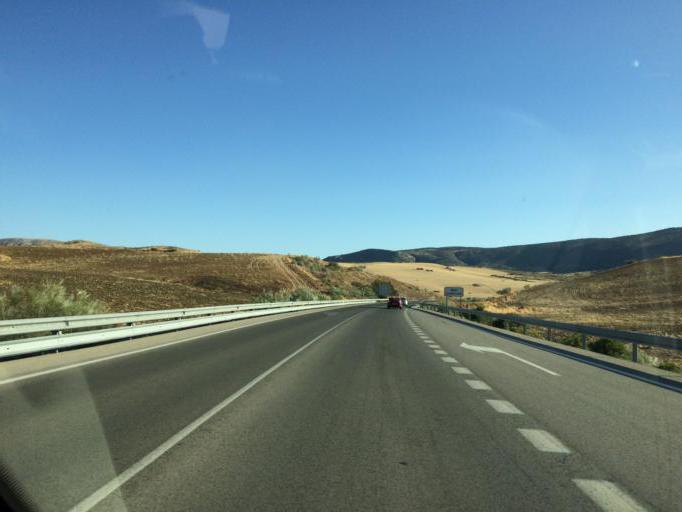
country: ES
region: Andalusia
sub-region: Provincia de Malaga
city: Ardales
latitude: 36.9413
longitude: -4.8668
